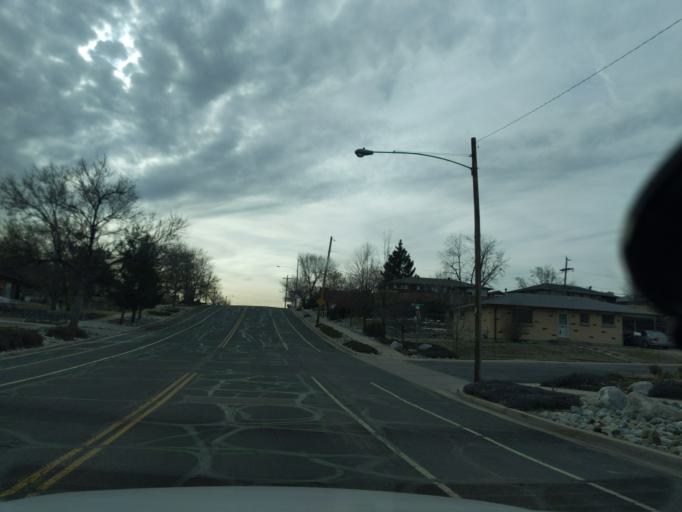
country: US
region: Colorado
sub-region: Adams County
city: Thornton
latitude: 39.8615
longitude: -104.9524
